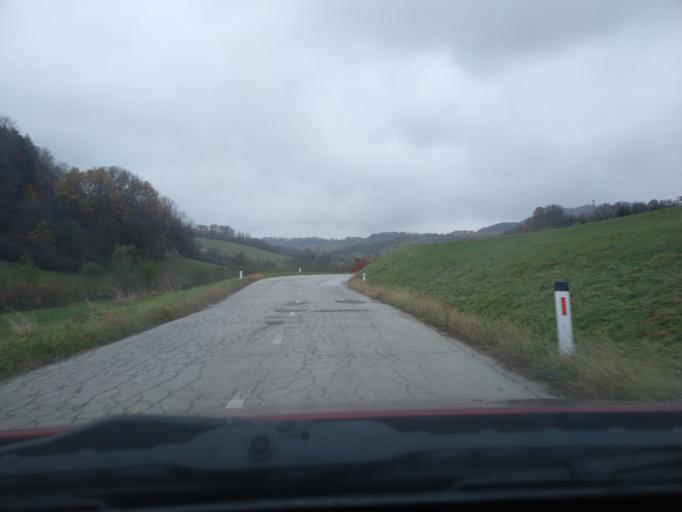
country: SI
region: Kungota
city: Zgornja Kungota
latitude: 46.6633
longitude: 15.6105
